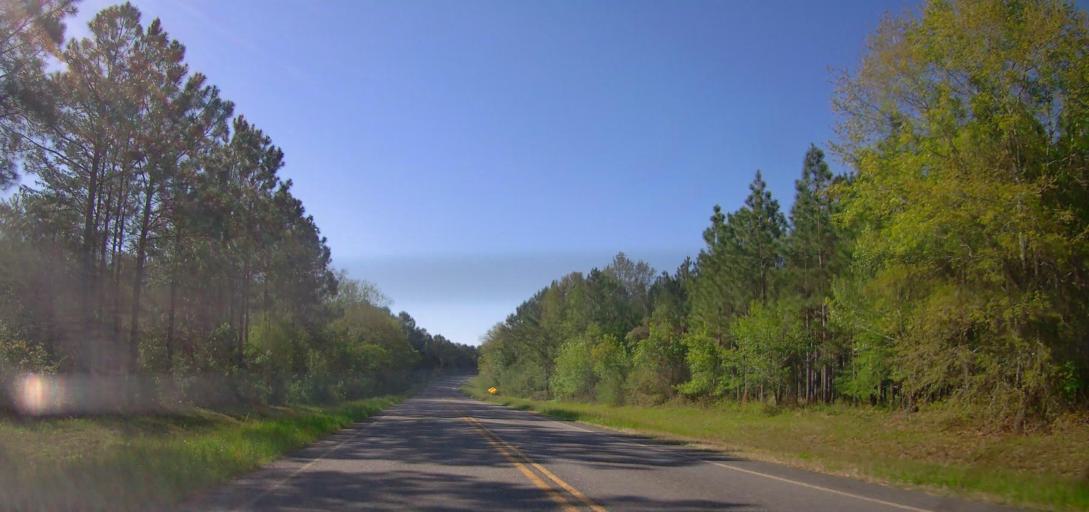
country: US
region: Georgia
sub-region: Wilcox County
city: Rochelle
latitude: 32.0099
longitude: -83.4910
